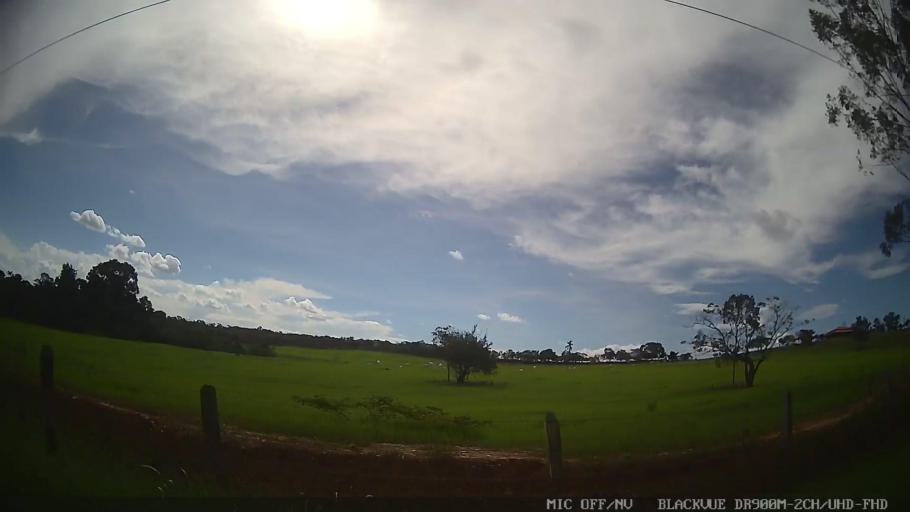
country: BR
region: Sao Paulo
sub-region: Conchas
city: Conchas
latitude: -22.9859
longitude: -47.9917
